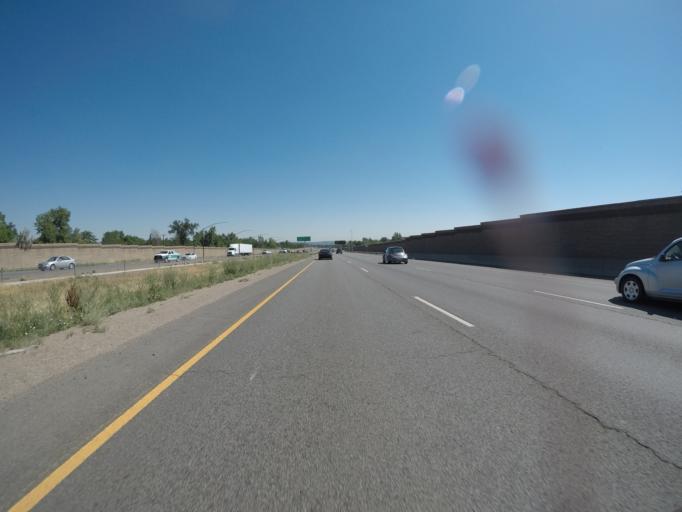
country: US
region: Colorado
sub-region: Jefferson County
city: Applewood
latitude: 39.7483
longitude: -105.1500
